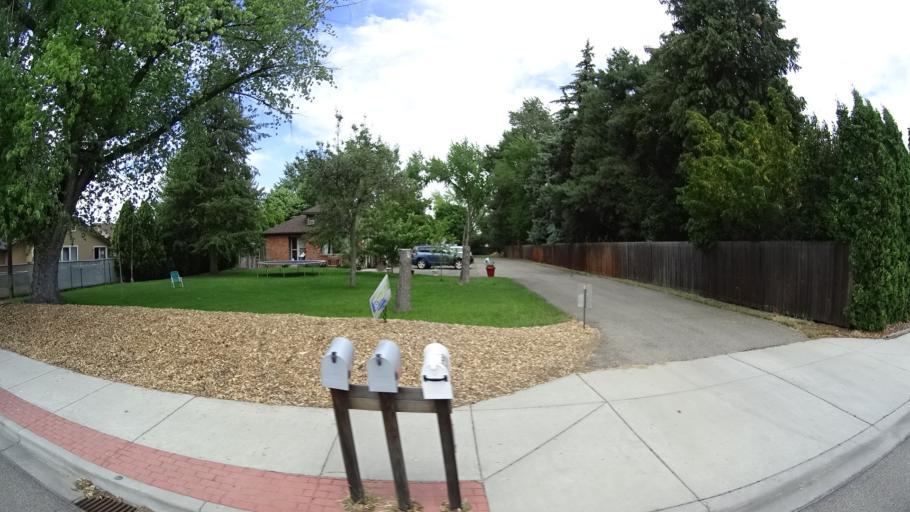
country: US
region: Idaho
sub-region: Ada County
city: Garden City
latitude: 43.6340
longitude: -116.2912
